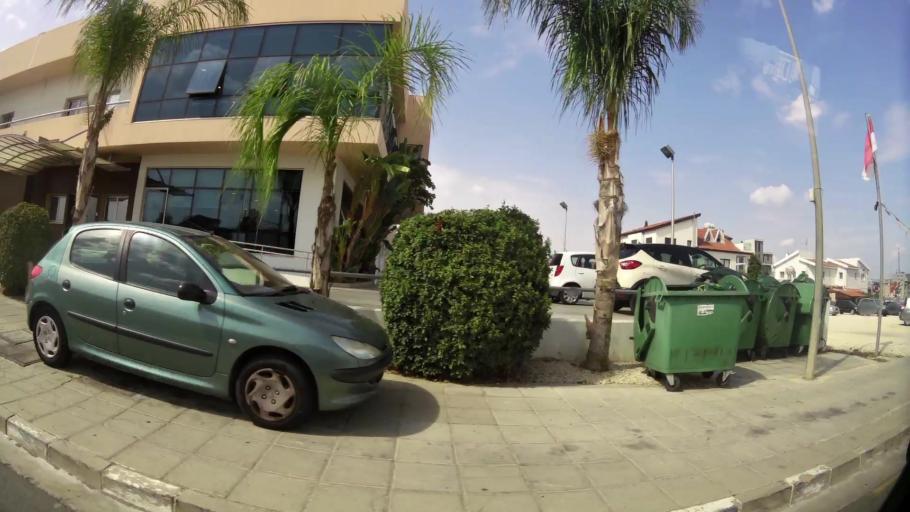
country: CY
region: Lefkosia
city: Tseri
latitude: 35.1205
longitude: 33.3344
